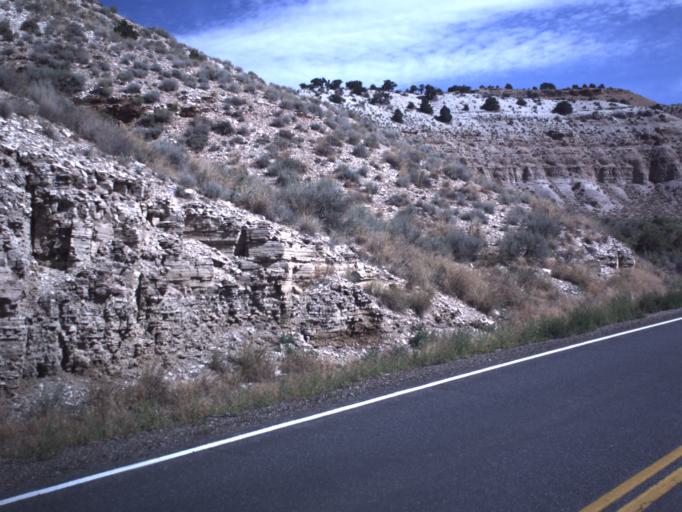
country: US
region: Utah
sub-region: Duchesne County
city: Duchesne
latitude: 40.1130
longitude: -110.4556
